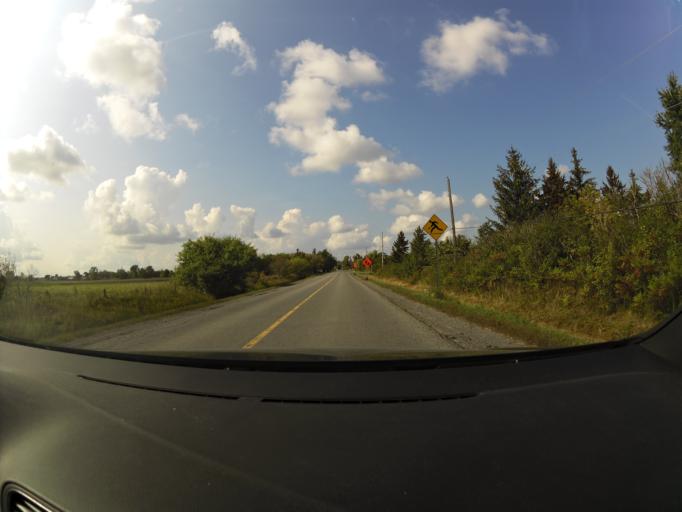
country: CA
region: Ontario
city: Arnprior
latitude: 45.3880
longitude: -76.1840
